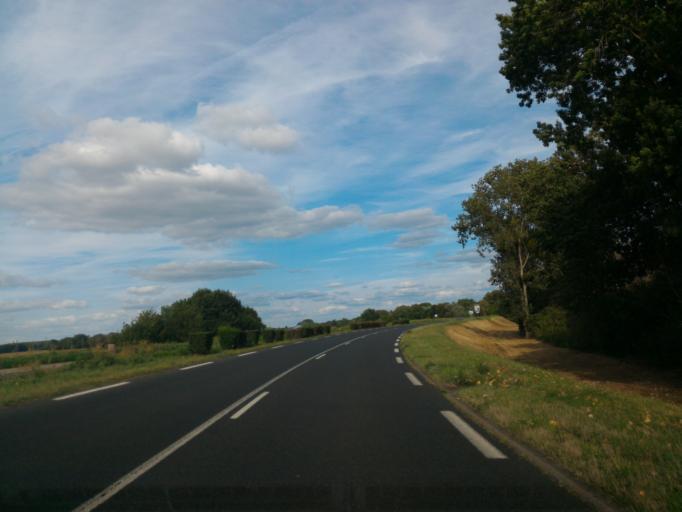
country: FR
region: Centre
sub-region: Departement d'Indre-et-Loire
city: Cangey
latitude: 47.4640
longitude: 1.0858
